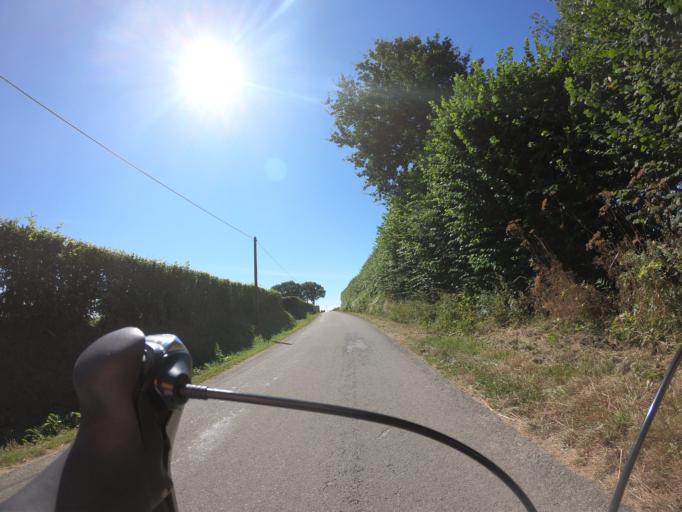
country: FR
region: Lower Normandy
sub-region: Departement de l'Orne
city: Saint-Denis-sur-Sarthon
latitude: 48.5172
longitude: -0.0829
